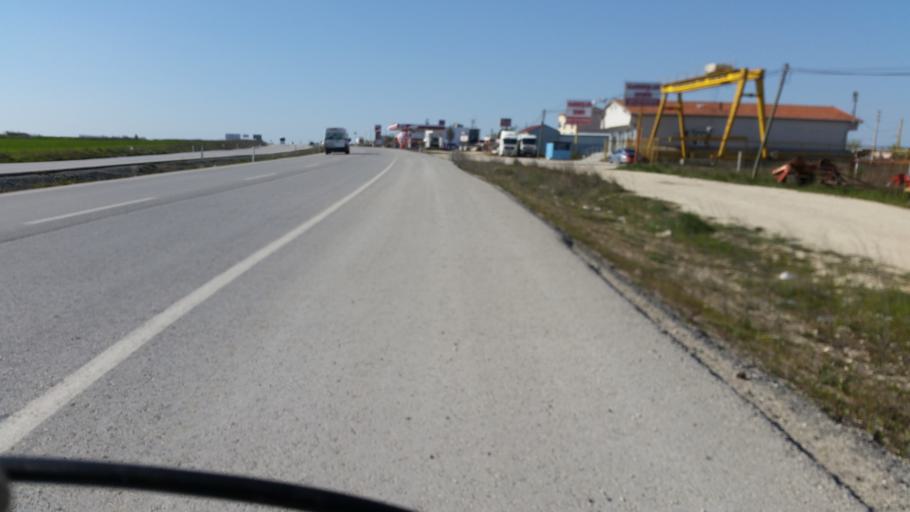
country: TR
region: Tekirdag
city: Cerkezkoey
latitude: 41.3394
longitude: 27.9662
